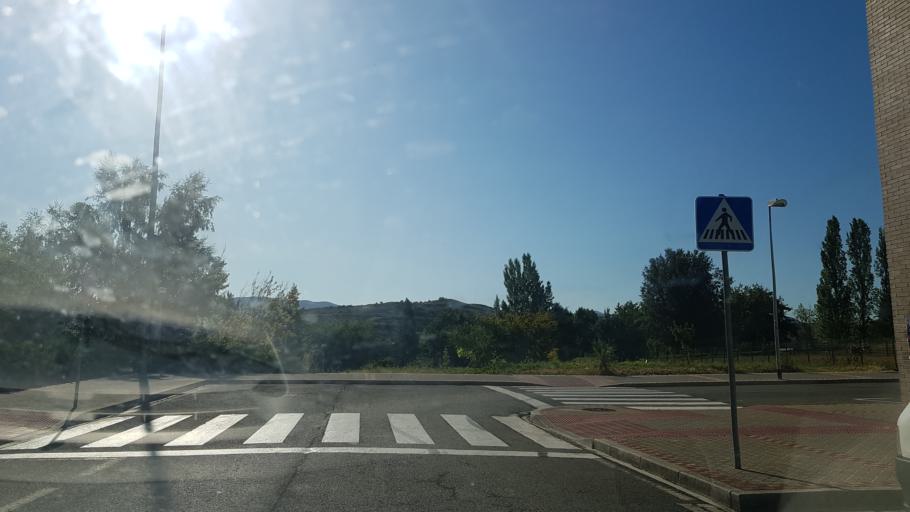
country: ES
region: Navarre
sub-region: Provincia de Navarra
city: Burlata
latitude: 42.8115
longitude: -1.6177
